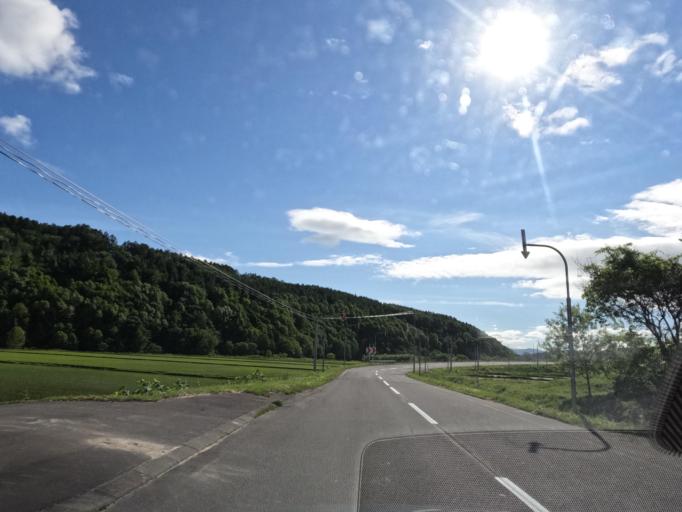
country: JP
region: Hokkaido
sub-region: Asahikawa-shi
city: Asahikawa
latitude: 43.6258
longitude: 142.5371
